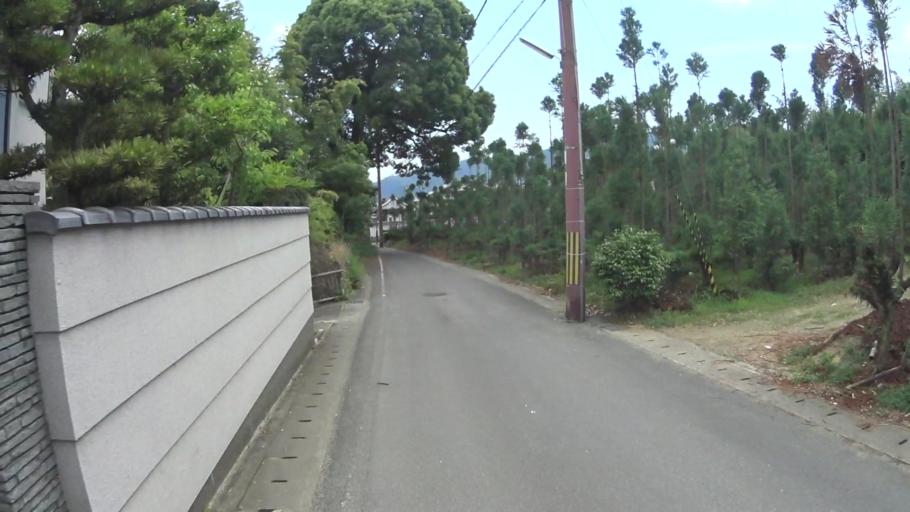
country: JP
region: Kyoto
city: Muko
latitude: 35.0307
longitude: 135.6760
